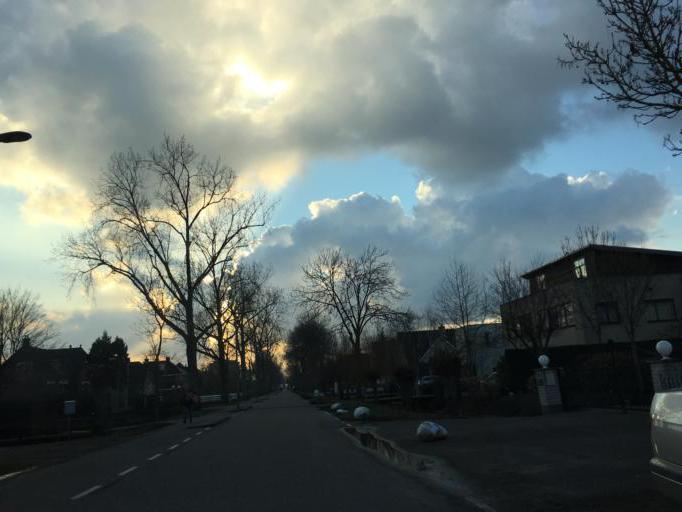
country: NL
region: South Holland
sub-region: Gemeente Rotterdam
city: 's-Gravenland
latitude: 51.9312
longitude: 4.5589
